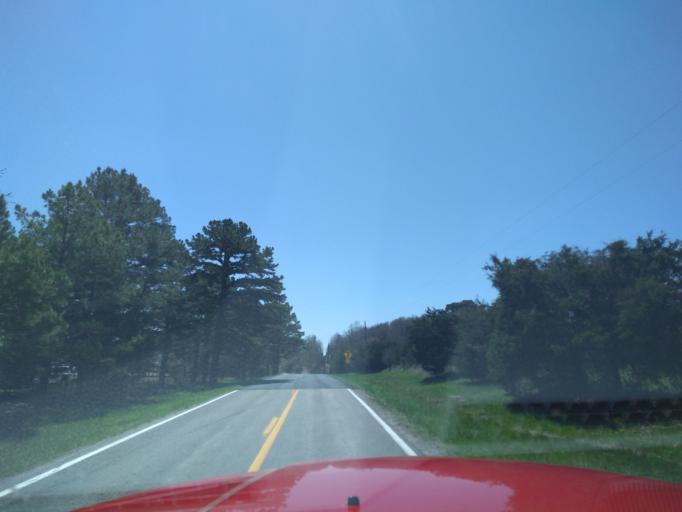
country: US
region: Arkansas
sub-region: Washington County
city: West Fork
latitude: 35.7986
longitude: -94.2552
